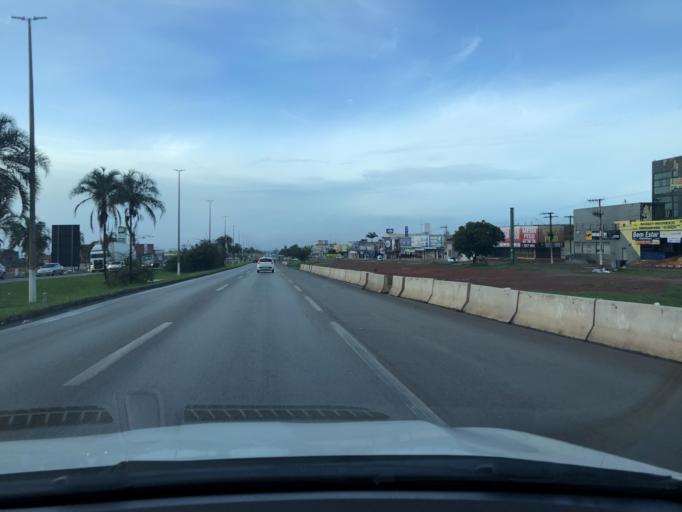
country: BR
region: Goias
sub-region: Luziania
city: Luziania
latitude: -16.0561
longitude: -47.9826
